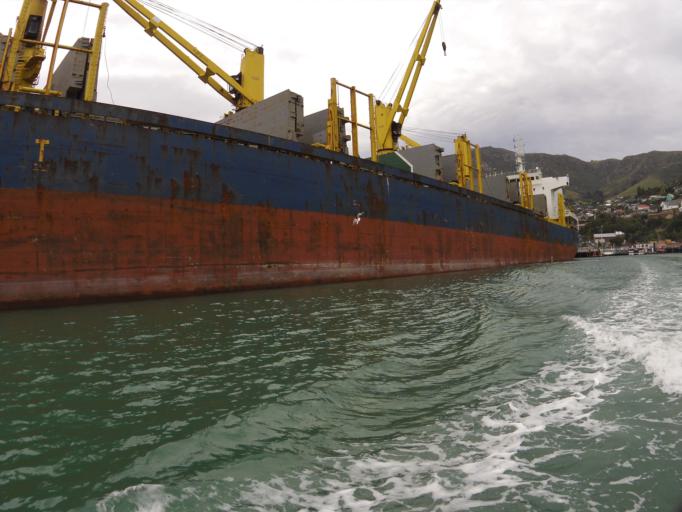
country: NZ
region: Canterbury
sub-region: Christchurch City
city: Christchurch
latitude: -43.6067
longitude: 172.7203
